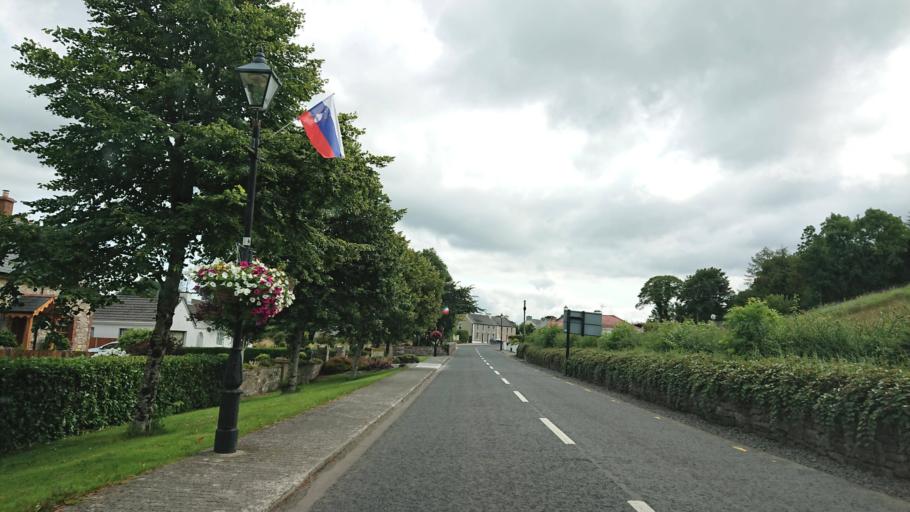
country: IE
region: Connaught
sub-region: County Leitrim
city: Carrick-on-Shannon
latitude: 54.0520
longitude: -8.1420
